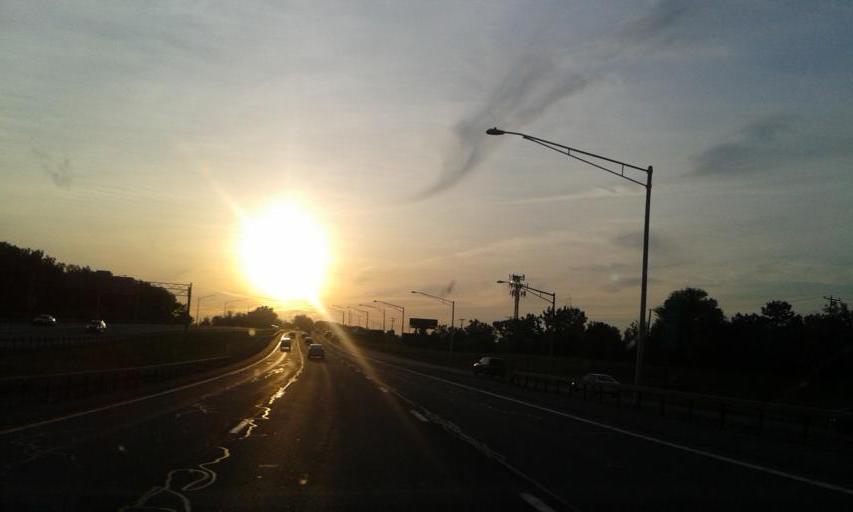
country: US
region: New York
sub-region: Onondaga County
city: Solvay
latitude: 43.0591
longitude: -76.1834
